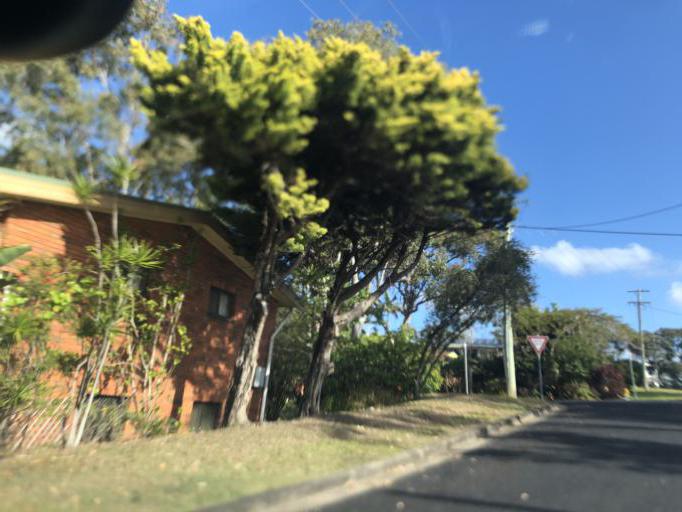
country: AU
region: New South Wales
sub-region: Coffs Harbour
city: Woolgoolga
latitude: -30.0958
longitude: 153.1970
